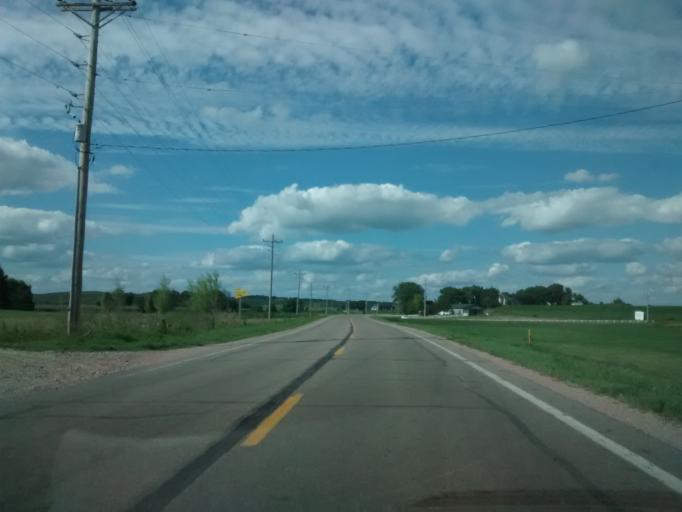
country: US
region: Iowa
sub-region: Woodbury County
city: Moville
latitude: 42.4949
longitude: -96.0722
